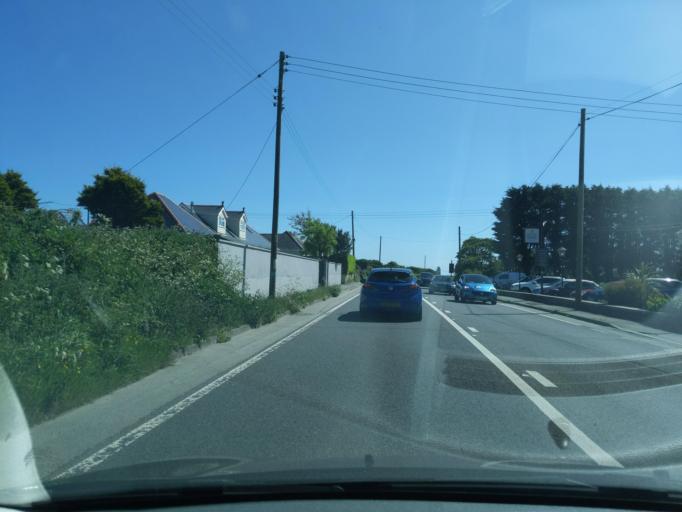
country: GB
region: England
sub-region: Cornwall
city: Wendron
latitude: 50.1593
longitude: -5.1860
